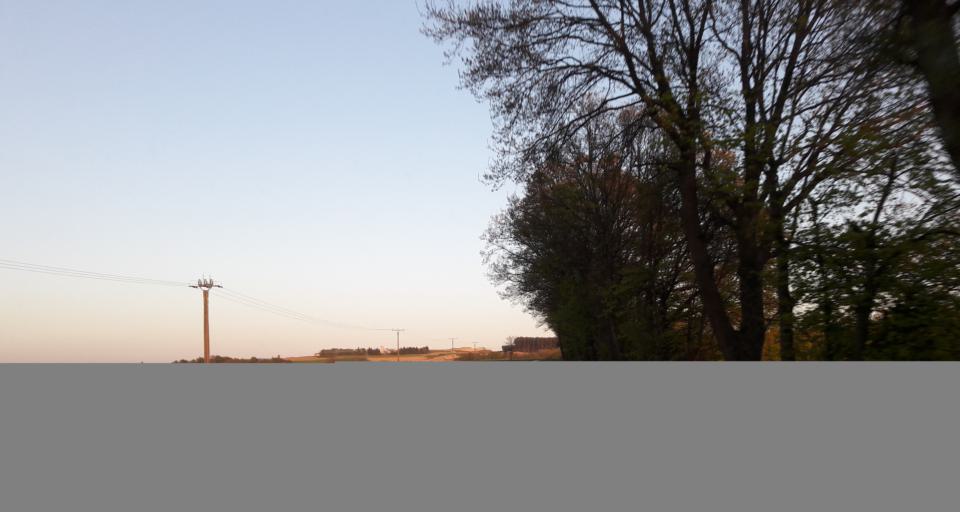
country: DE
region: Rheinland-Pfalz
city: Longkamp
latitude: 49.8831
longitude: 7.0958
